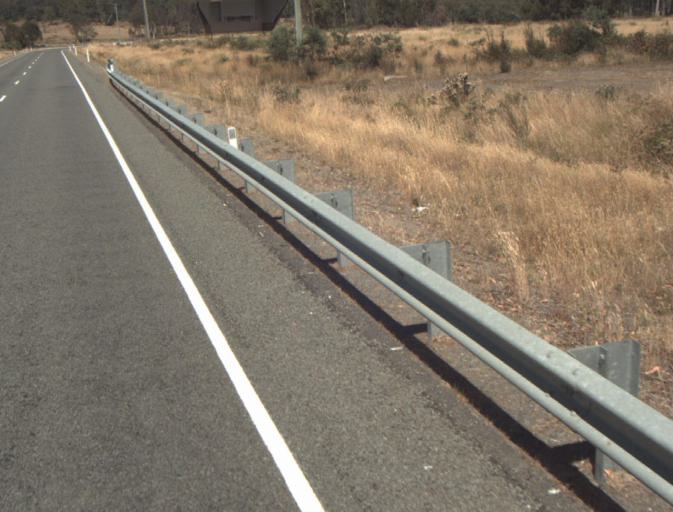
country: AU
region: Tasmania
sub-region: Launceston
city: Newstead
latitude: -41.3578
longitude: 147.3381
